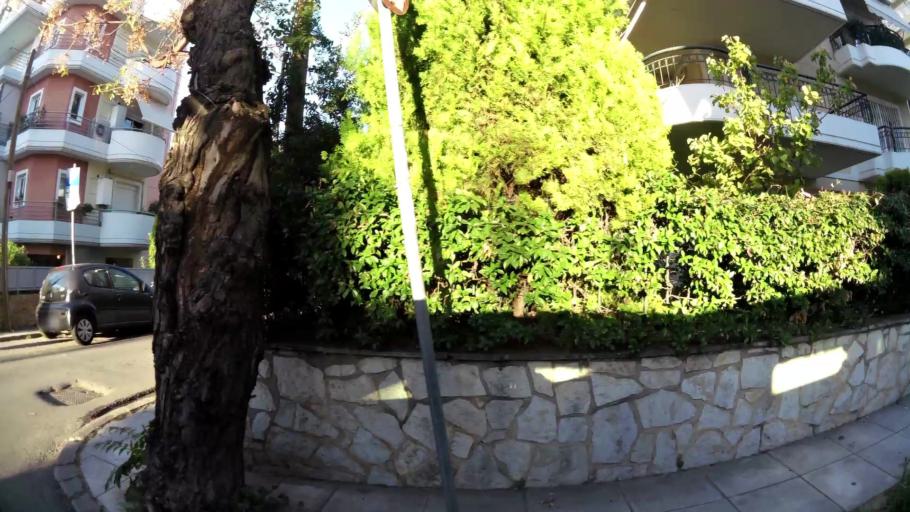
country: GR
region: Attica
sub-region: Nomarchia Athinas
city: Marousi
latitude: 38.0504
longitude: 23.8016
